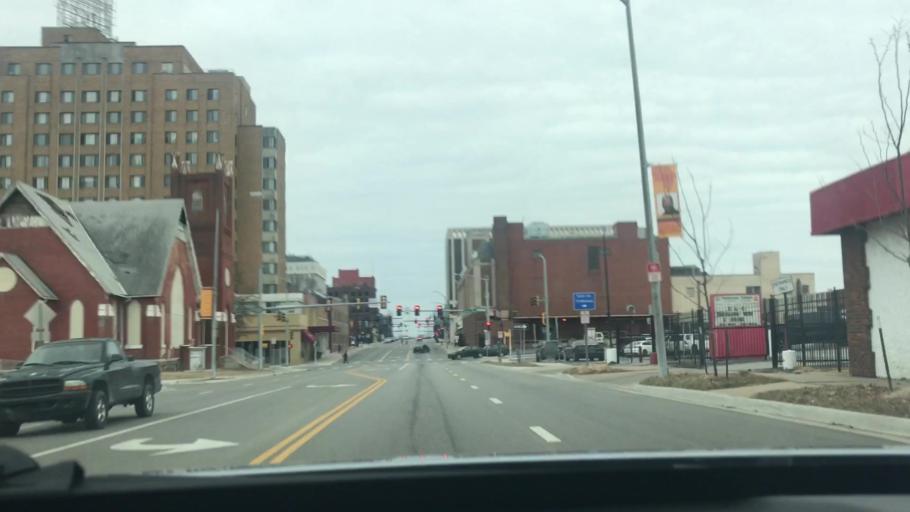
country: US
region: Kansas
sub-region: Wyandotte County
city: Kansas City
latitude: 39.1174
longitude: -94.6269
